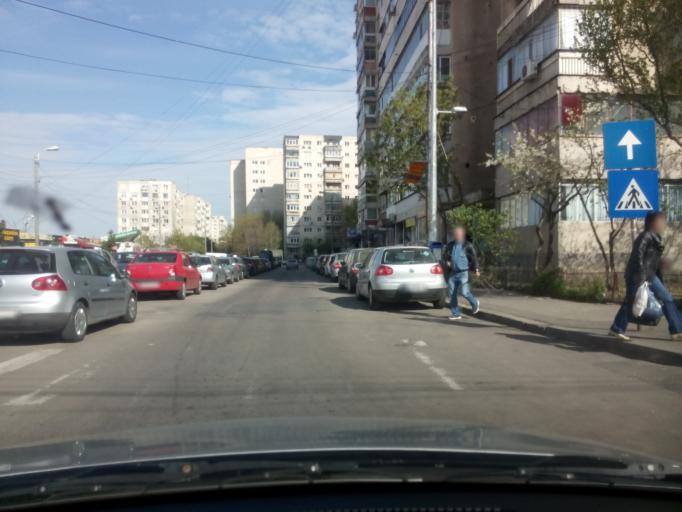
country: RO
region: Ilfov
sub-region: Comuna Fundeni-Dobroesti
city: Fundeni
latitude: 44.4445
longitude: 26.1580
